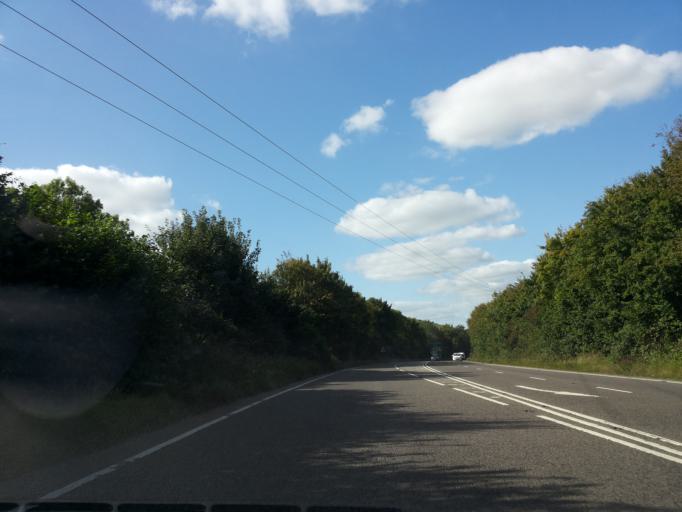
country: GB
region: England
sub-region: Wiltshire
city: Warminster
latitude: 51.1975
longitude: -2.2120
